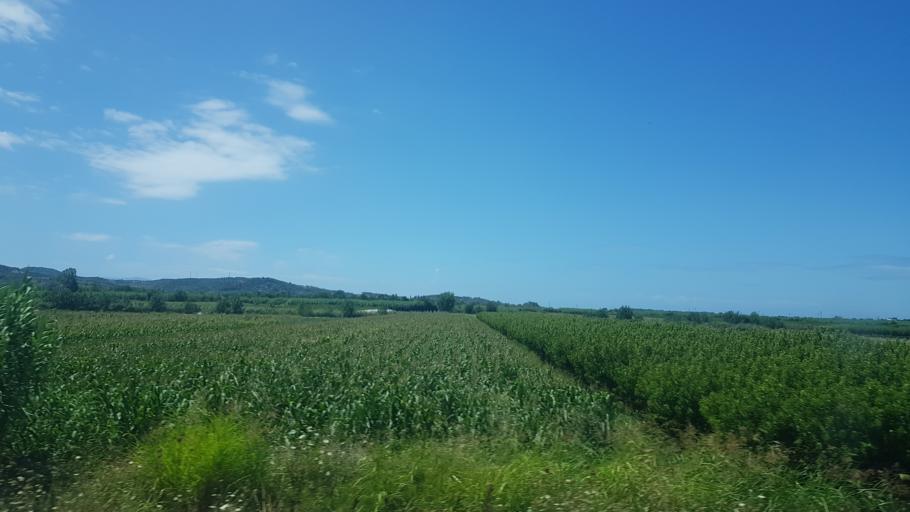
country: AL
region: Fier
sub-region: Rrethi i Fierit
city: Frakulla e Madhe
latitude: 40.6191
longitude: 19.5183
